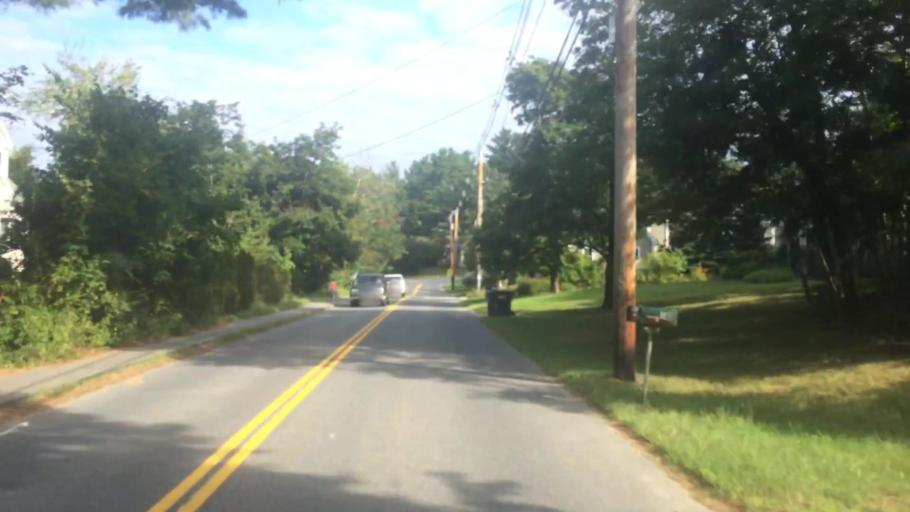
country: US
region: Massachusetts
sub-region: Middlesex County
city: Acton
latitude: 42.4734
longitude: -71.4590
